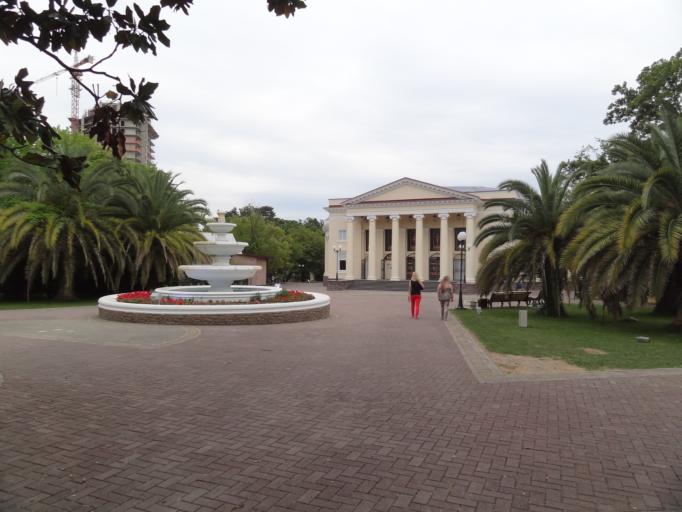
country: RU
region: Krasnodarskiy
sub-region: Sochi City
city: Sochi
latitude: 43.5695
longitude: 39.7332
